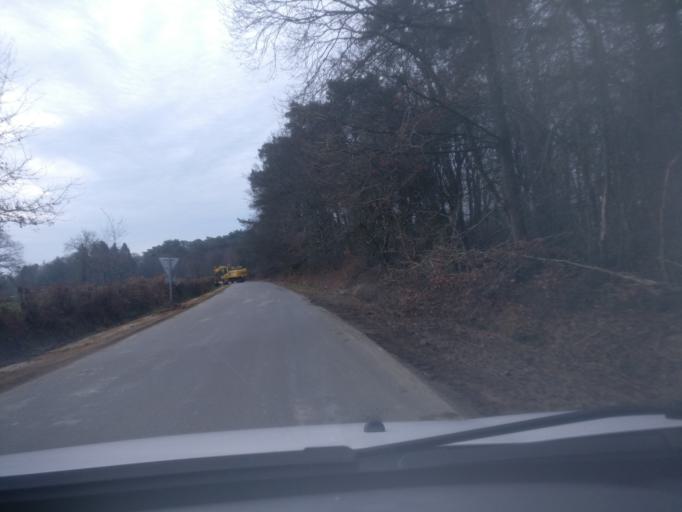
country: FR
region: Brittany
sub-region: Departement d'Ille-et-Vilaine
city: Liffre
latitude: 48.1934
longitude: -1.5261
